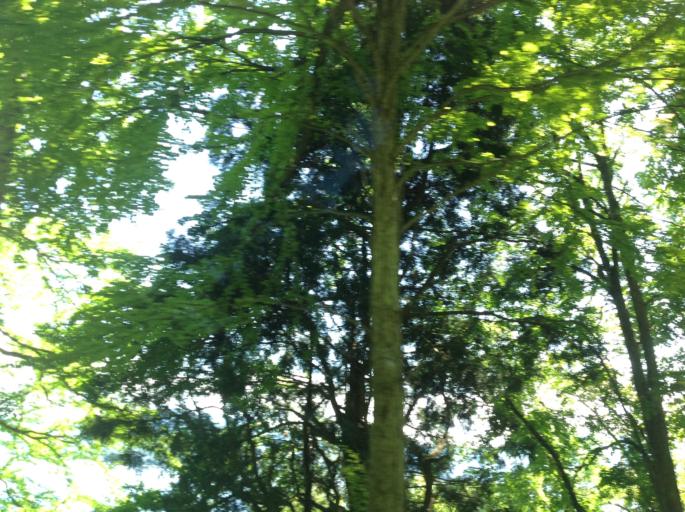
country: JP
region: Akita
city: Kakunodatemachi
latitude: 39.7088
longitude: 140.6379
